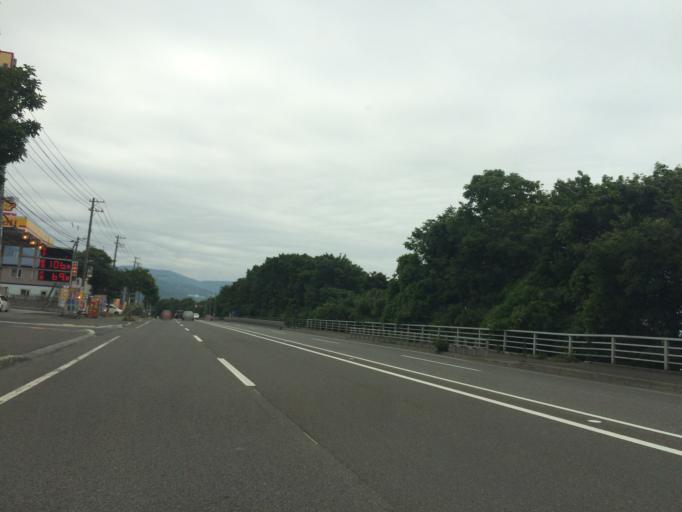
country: JP
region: Hokkaido
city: Sapporo
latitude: 43.1313
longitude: 141.2040
